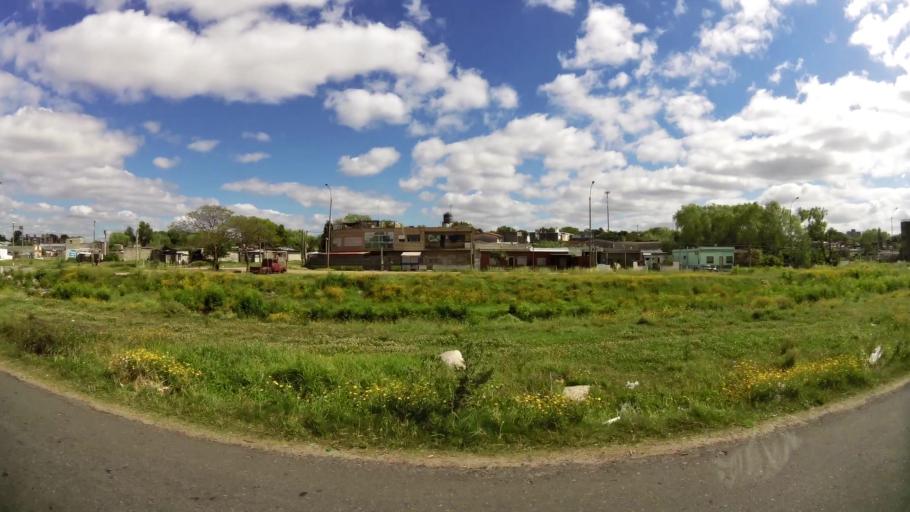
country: UY
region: Montevideo
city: Montevideo
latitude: -34.8822
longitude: -56.1275
